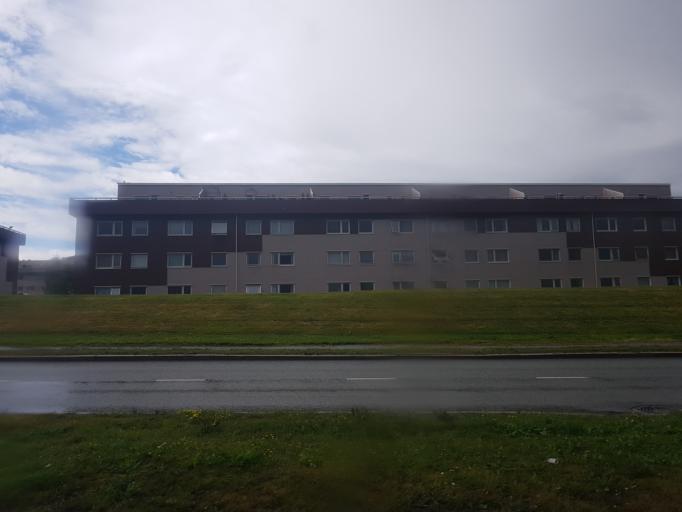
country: NO
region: Sor-Trondelag
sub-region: Trondheim
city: Trondheim
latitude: 63.4104
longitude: 10.3611
